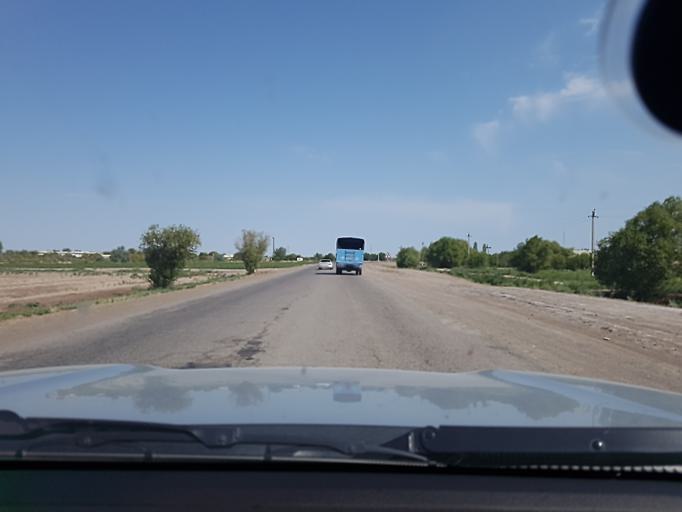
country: TM
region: Dasoguz
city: Boldumsaz
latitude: 42.1575
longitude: 59.6090
